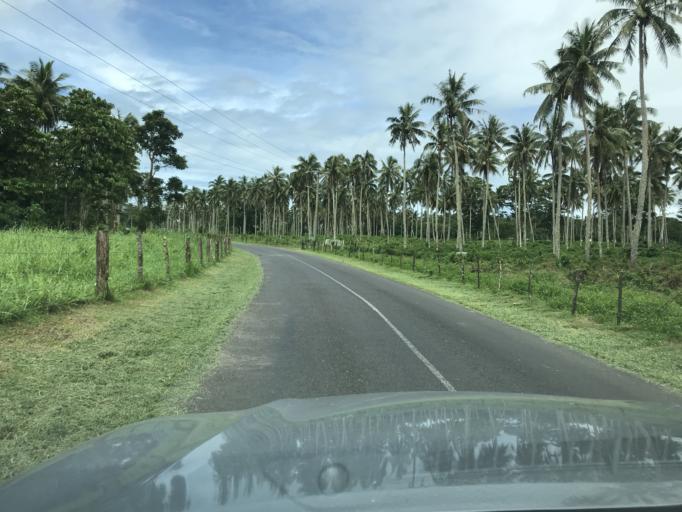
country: WS
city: Fasito`outa
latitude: -13.8726
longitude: -171.9156
